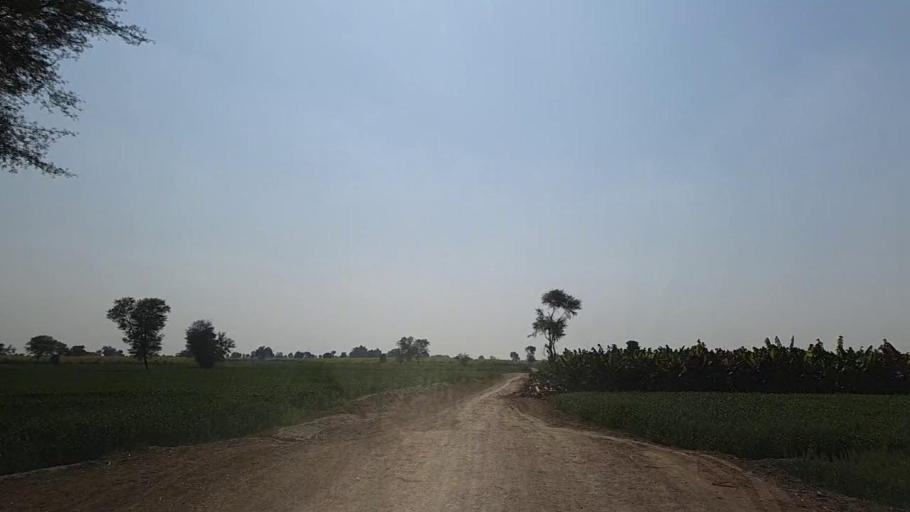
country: PK
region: Sindh
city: Daur
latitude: 26.4892
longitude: 68.2596
